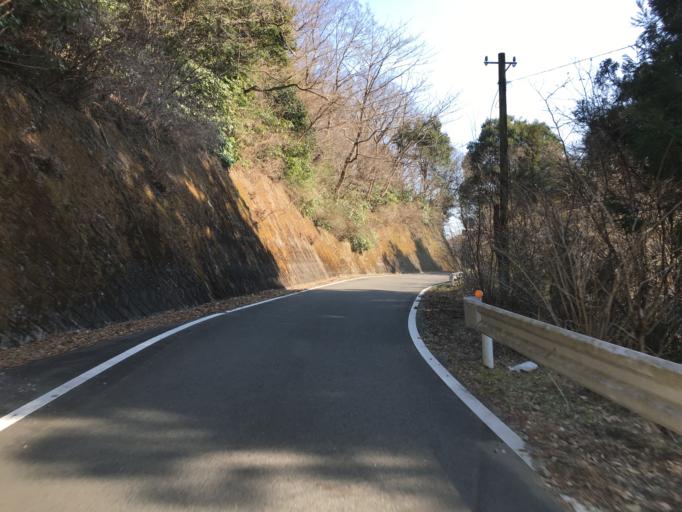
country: JP
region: Ibaraki
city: Kitaibaraki
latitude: 36.7793
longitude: 140.6785
